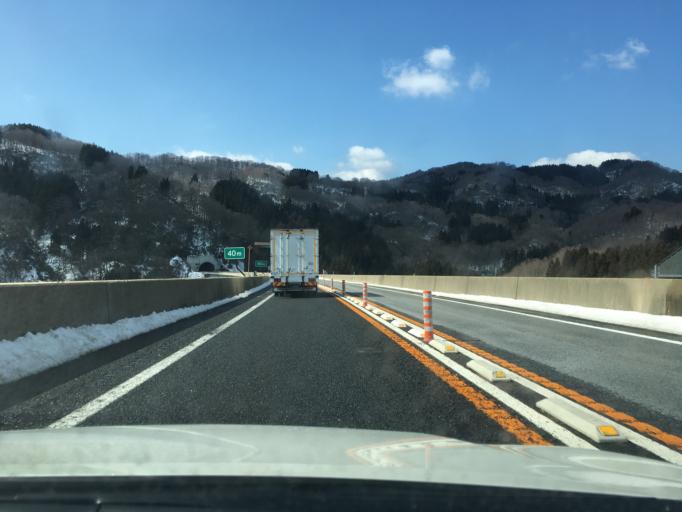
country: JP
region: Yamagata
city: Tsuruoka
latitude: 38.5919
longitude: 139.8856
